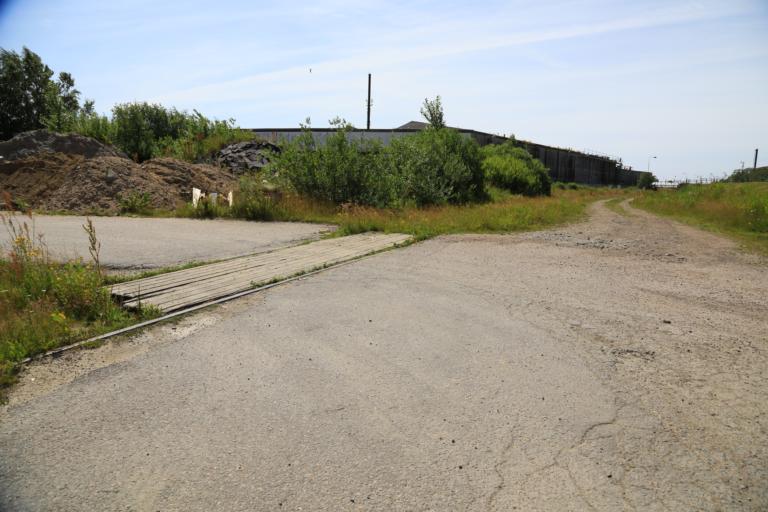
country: SE
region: Halland
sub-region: Varbergs Kommun
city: Varberg
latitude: 57.1196
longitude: 12.2546
